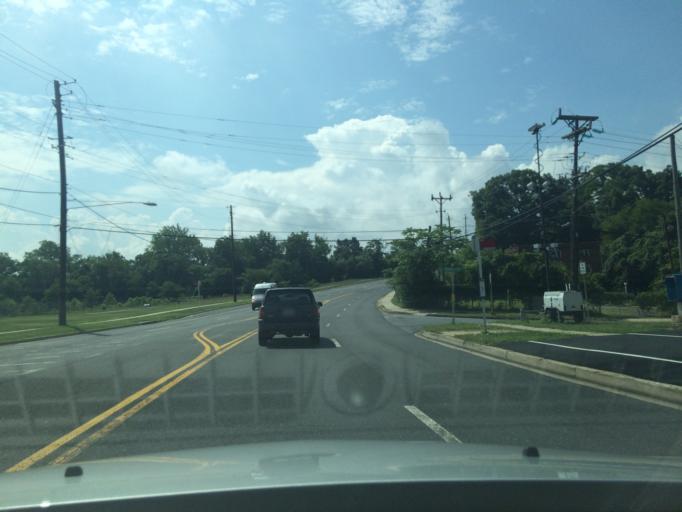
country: US
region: Maryland
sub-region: Prince George's County
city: Coral Hills
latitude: 38.8691
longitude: -76.9182
